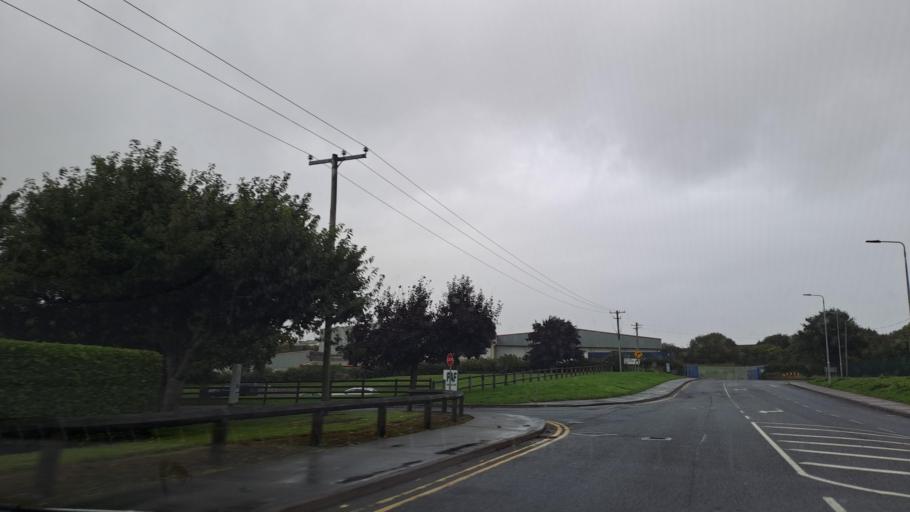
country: IE
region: Ulster
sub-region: County Monaghan
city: Carrickmacross
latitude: 53.9812
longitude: -6.7222
